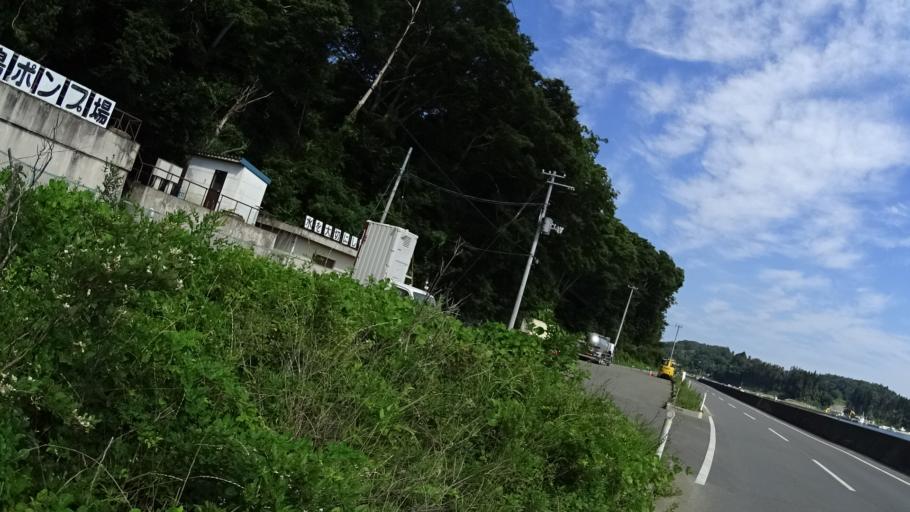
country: JP
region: Iwate
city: Ofunato
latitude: 38.8677
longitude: 141.6060
